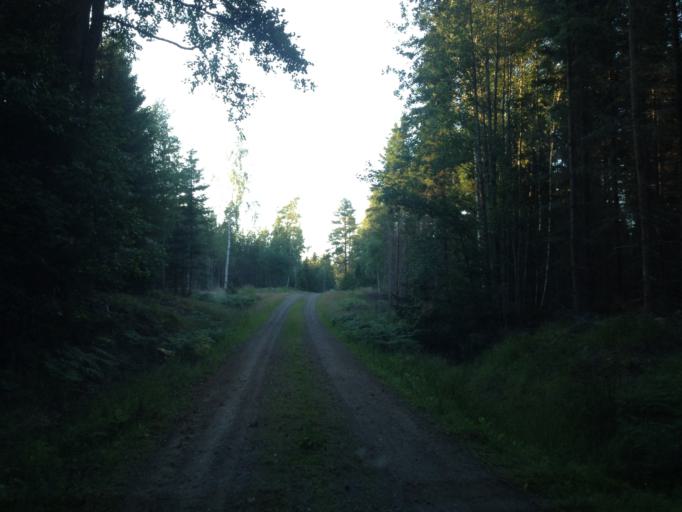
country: SE
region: Kalmar
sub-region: Vasterviks Kommun
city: Overum
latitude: 57.9946
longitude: 16.1693
